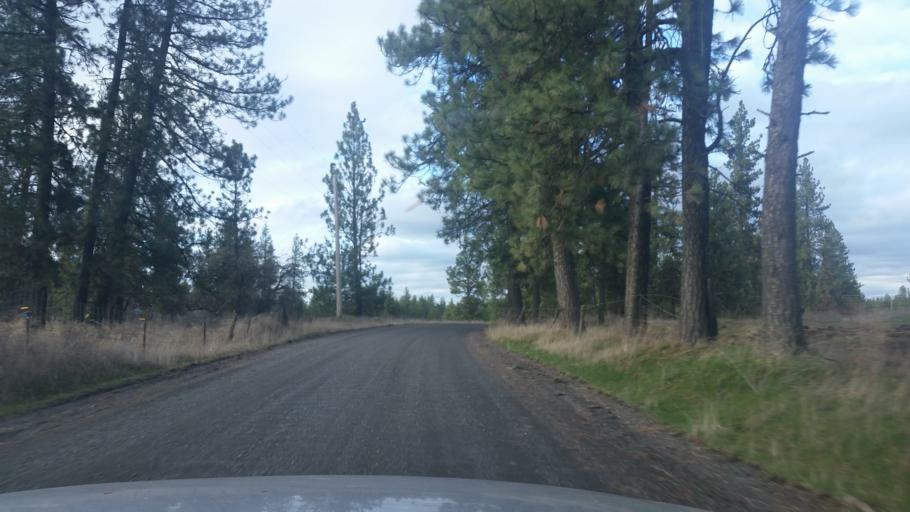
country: US
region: Washington
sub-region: Spokane County
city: Cheney
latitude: 47.4278
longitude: -117.4660
